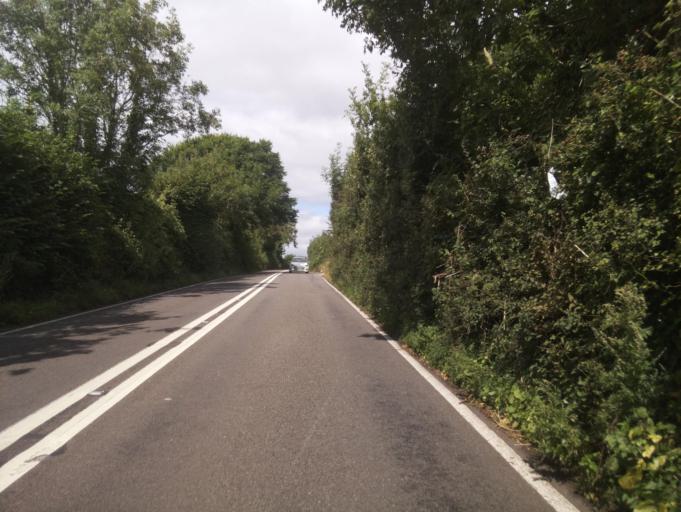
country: GB
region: England
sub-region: Devon
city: Teignmouth
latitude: 50.5096
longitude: -3.5186
